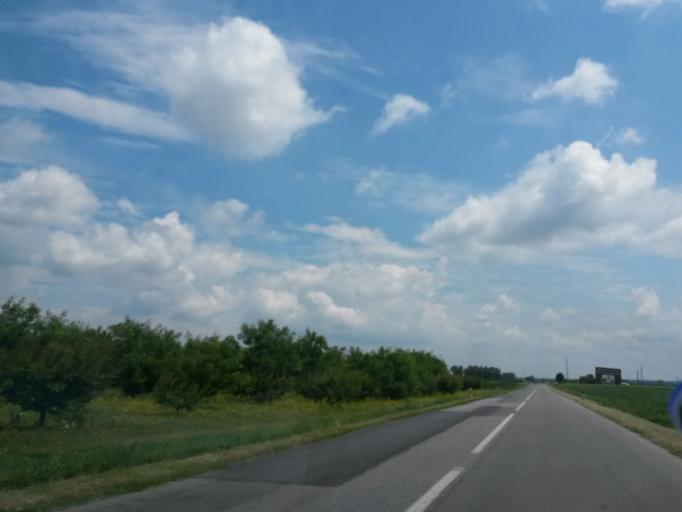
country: HR
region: Osjecko-Baranjska
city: Dalj
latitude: 45.5057
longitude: 18.9454
